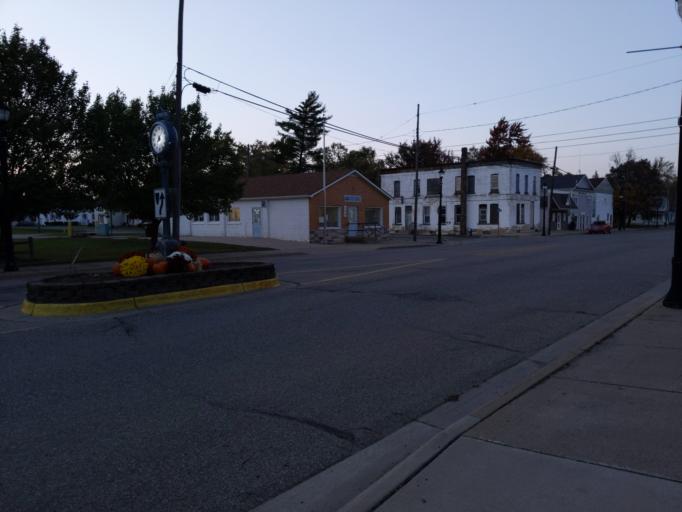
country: US
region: Michigan
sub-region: Clinton County
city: Fowler
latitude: 43.0031
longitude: -84.7395
